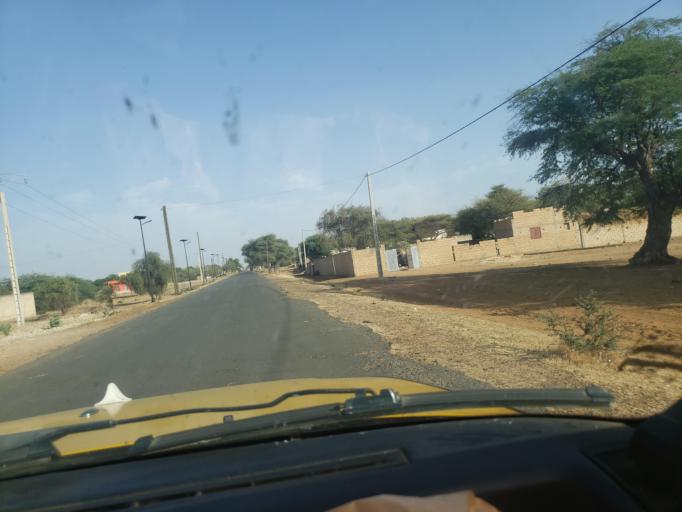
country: SN
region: Louga
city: Louga
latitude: 15.5124
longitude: -15.9927
